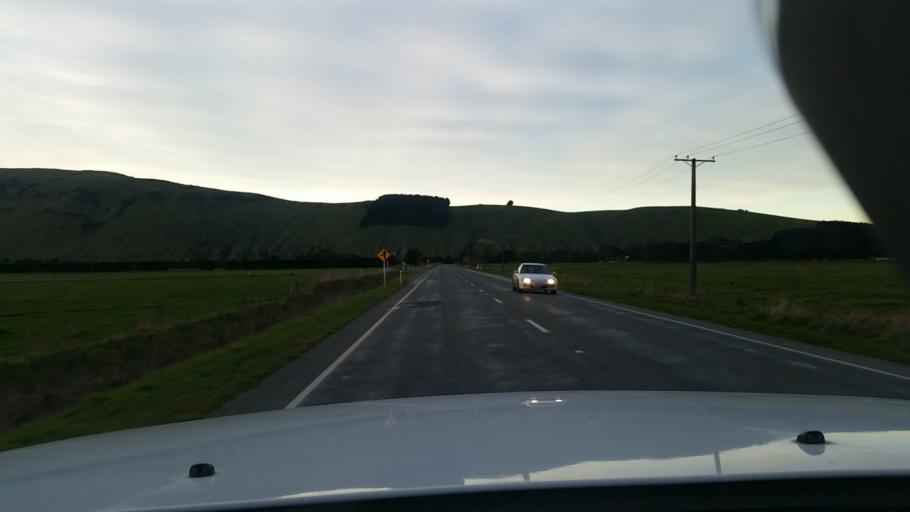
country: NZ
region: Canterbury
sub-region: Selwyn District
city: Lincoln
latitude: -43.7287
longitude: 172.6084
